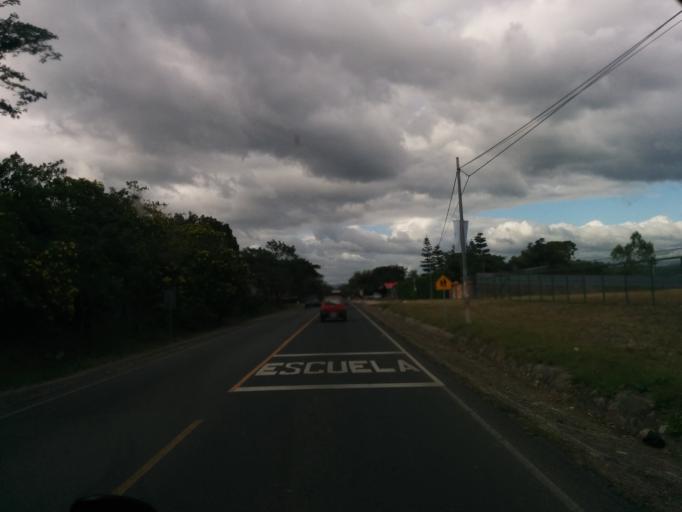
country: NI
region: Esteli
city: Esteli
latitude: 13.1228
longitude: -86.3631
